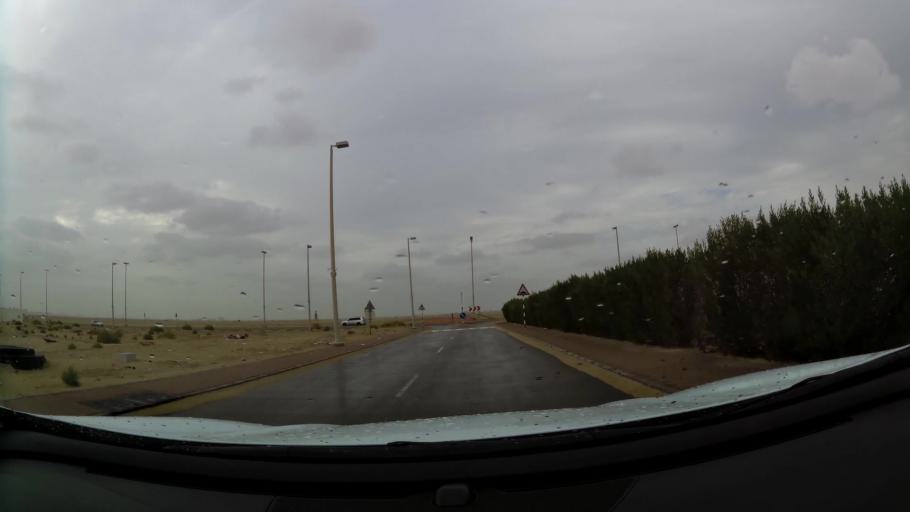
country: AE
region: Abu Dhabi
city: Abu Dhabi
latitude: 24.3667
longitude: 54.6221
